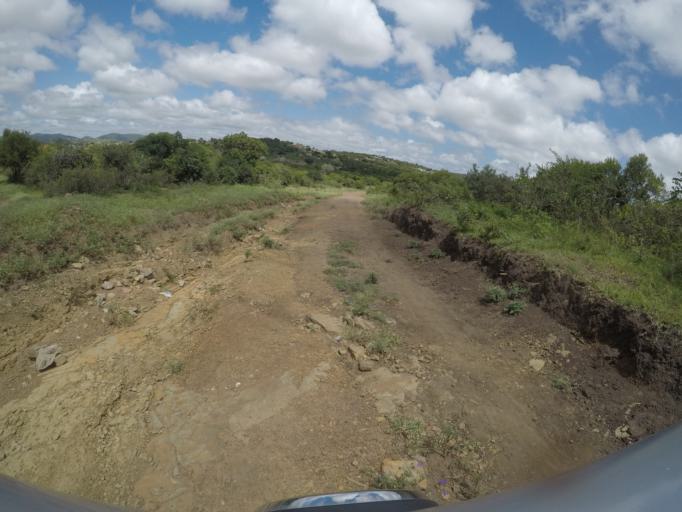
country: ZA
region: KwaZulu-Natal
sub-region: uThungulu District Municipality
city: Empangeni
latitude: -28.5789
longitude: 31.8379
